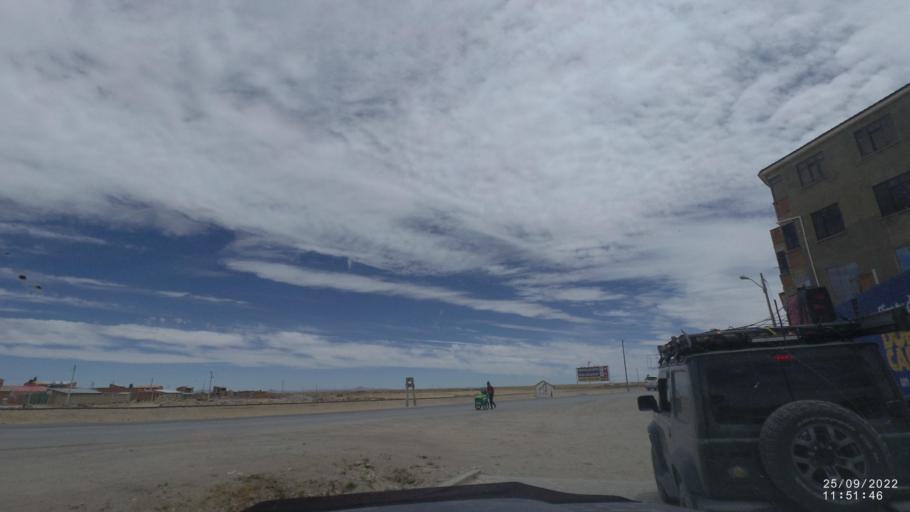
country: BO
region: Oruro
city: Challapata
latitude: -18.8927
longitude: -66.7792
